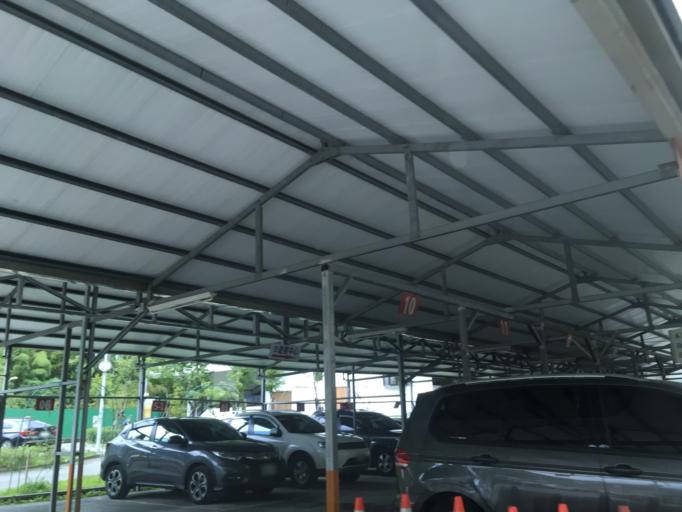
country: TW
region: Taiwan
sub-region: Yunlin
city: Douliu
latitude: 23.5598
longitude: 120.6007
